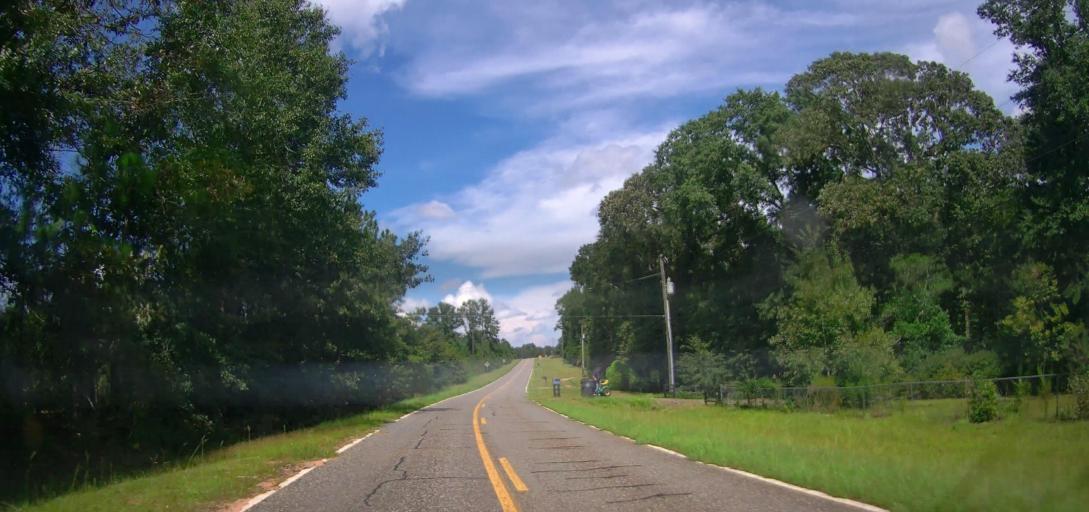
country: US
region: Georgia
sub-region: Peach County
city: Fort Valley
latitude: 32.5188
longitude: -83.8289
